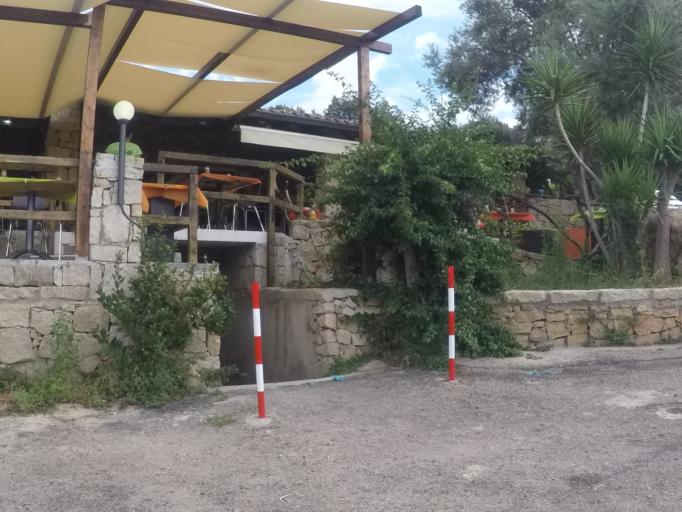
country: IT
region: Sardinia
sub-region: Provincia di Olbia-Tempio
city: Porto Cervo
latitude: 41.1405
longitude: 9.4753
